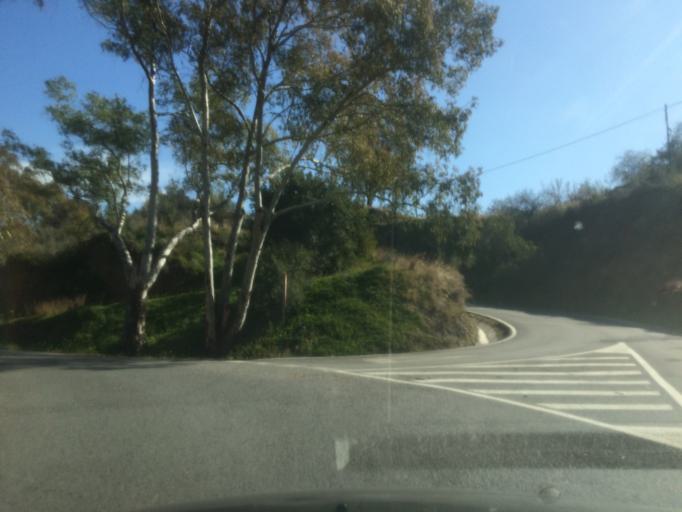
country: ES
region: Andalusia
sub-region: Provincia de Malaga
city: Malaga
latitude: 36.7740
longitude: -4.4292
